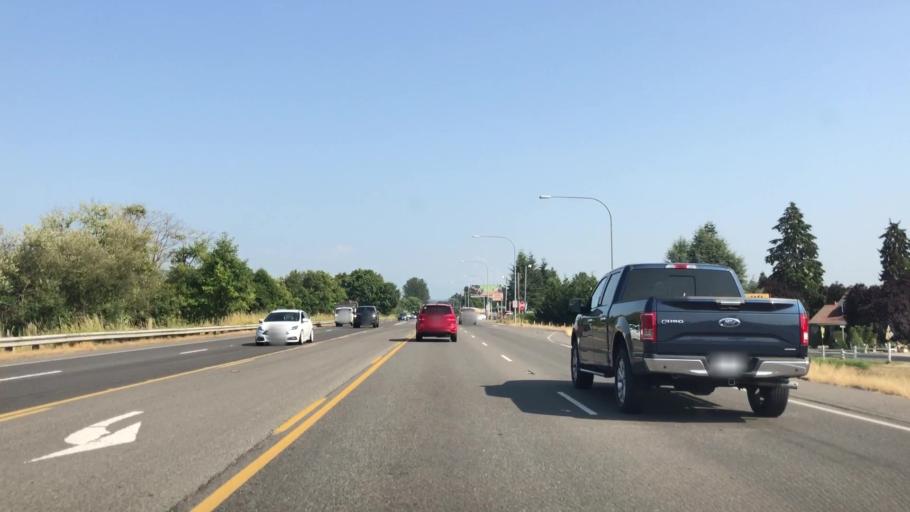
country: US
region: Washington
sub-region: Pierce County
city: Fife
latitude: 47.2178
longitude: -122.3495
